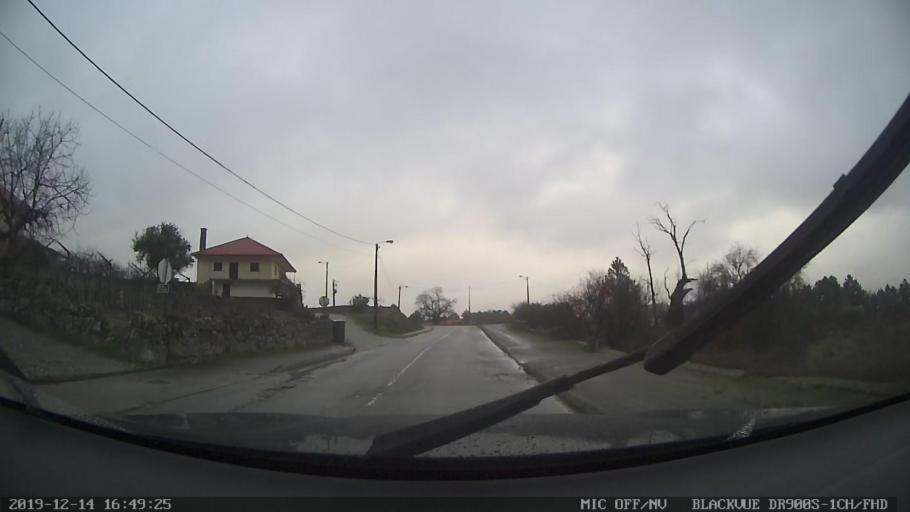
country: PT
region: Vila Real
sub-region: Murca
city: Murca
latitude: 41.4089
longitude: -7.5009
